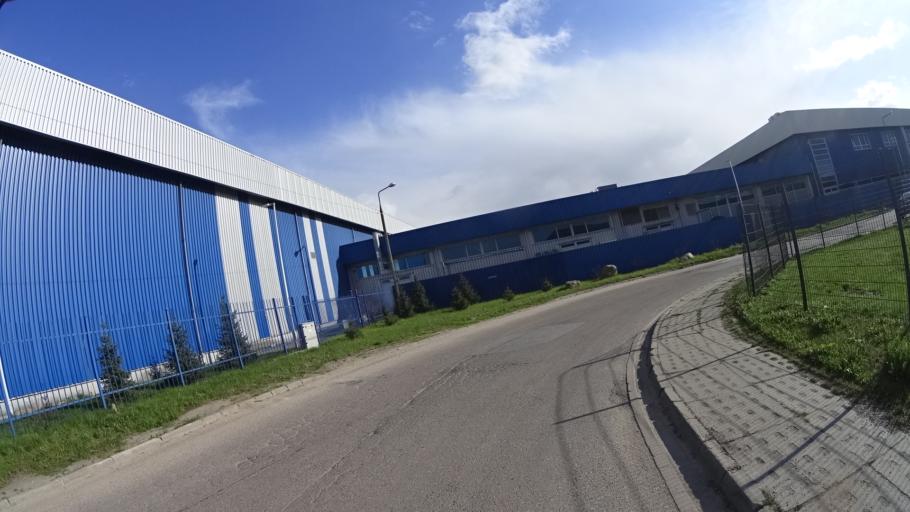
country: PL
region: Masovian Voivodeship
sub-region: Powiat warszawski zachodni
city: Babice
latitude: 52.2829
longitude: 20.8706
